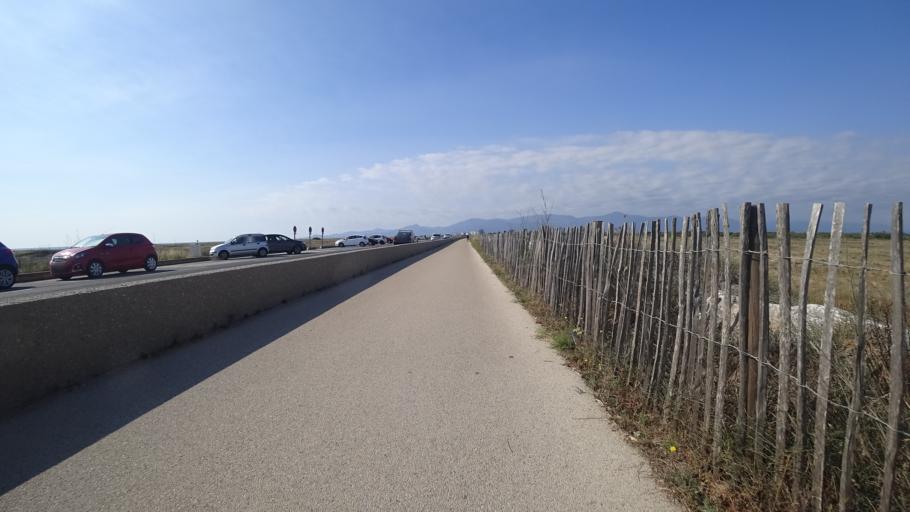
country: FR
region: Languedoc-Roussillon
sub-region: Departement des Pyrenees-Orientales
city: Saint-Cyprien-Plage
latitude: 42.6543
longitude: 3.0329
